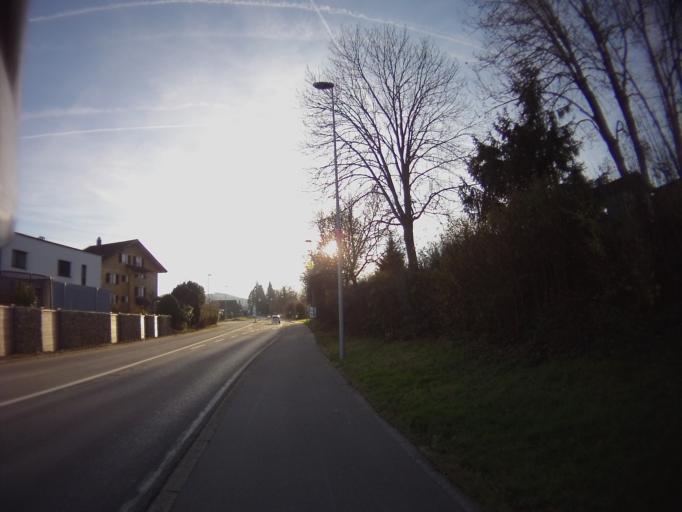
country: CH
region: Zug
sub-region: Zug
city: Cham
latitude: 47.1674
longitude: 8.4493
